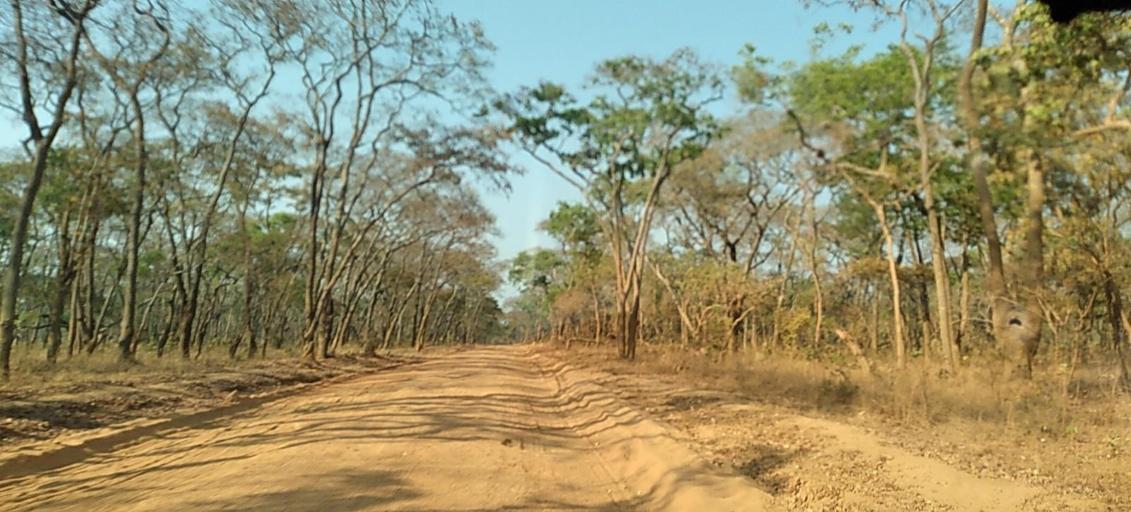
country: ZM
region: North-Western
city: Kasempa
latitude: -13.5932
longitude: 25.9826
